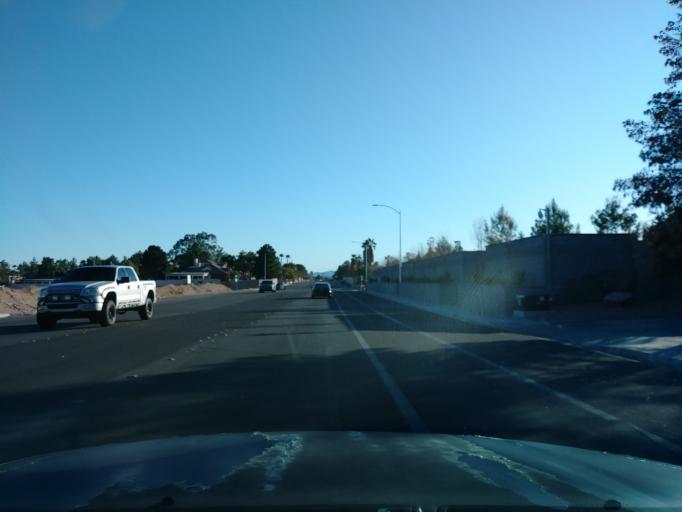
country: US
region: Nevada
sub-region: Clark County
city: Spring Valley
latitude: 36.1507
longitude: -115.2706
